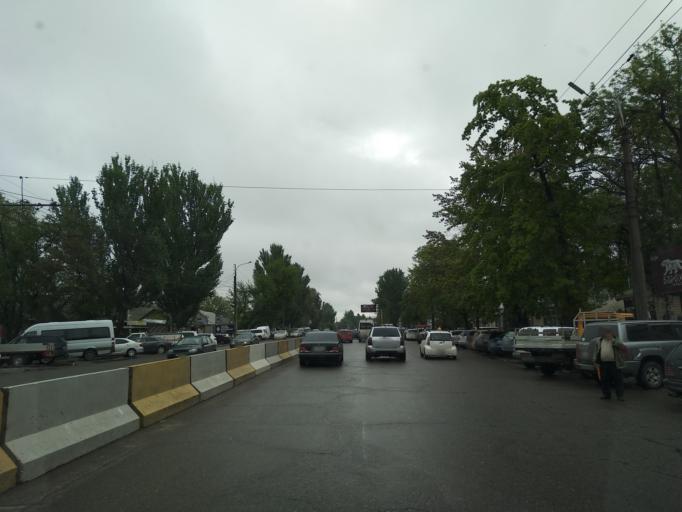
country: KG
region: Chuy
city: Lebedinovka
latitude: 42.8884
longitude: 74.6398
